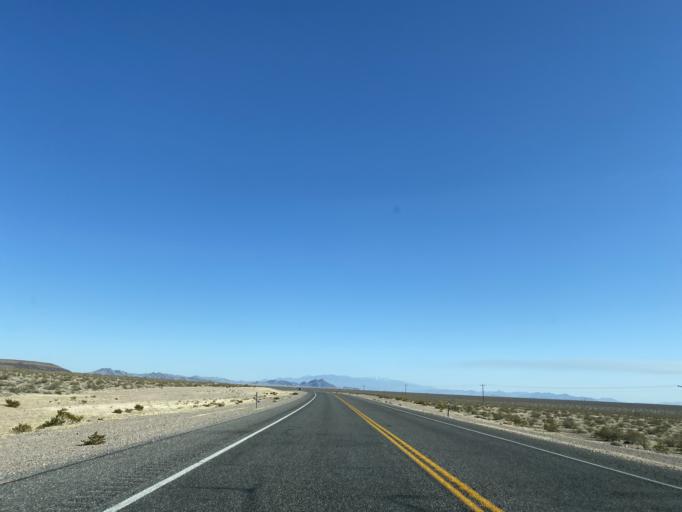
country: US
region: Nevada
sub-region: Nye County
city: Beatty
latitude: 36.6775
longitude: -116.5361
